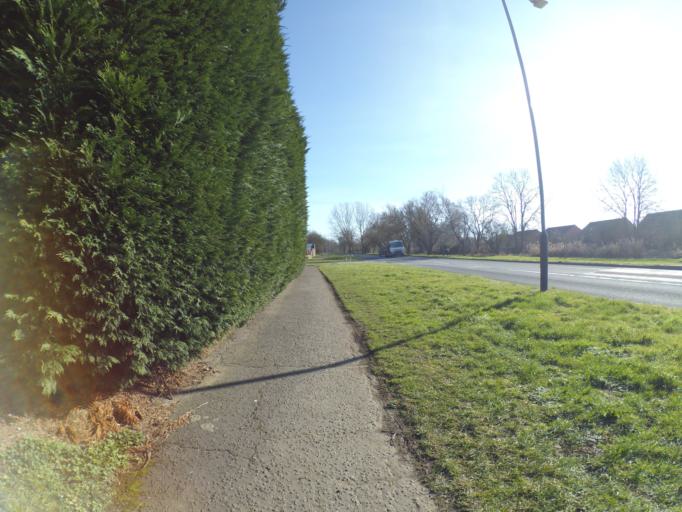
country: GB
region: England
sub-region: Warwickshire
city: Rugby
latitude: 52.3872
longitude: -1.2478
